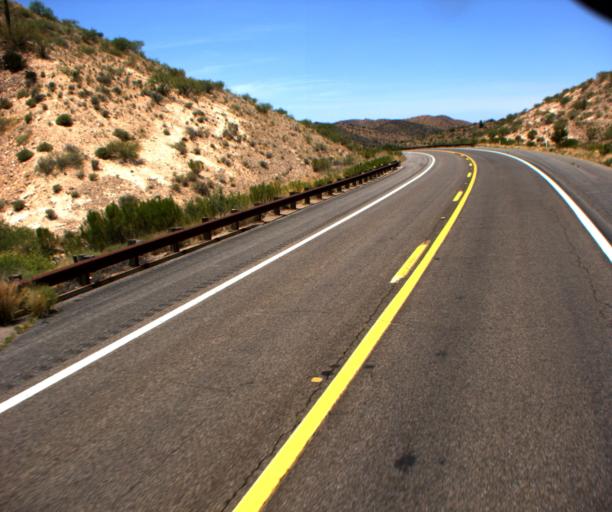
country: US
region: Arizona
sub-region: Gila County
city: Claypool
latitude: 33.4930
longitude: -110.8633
